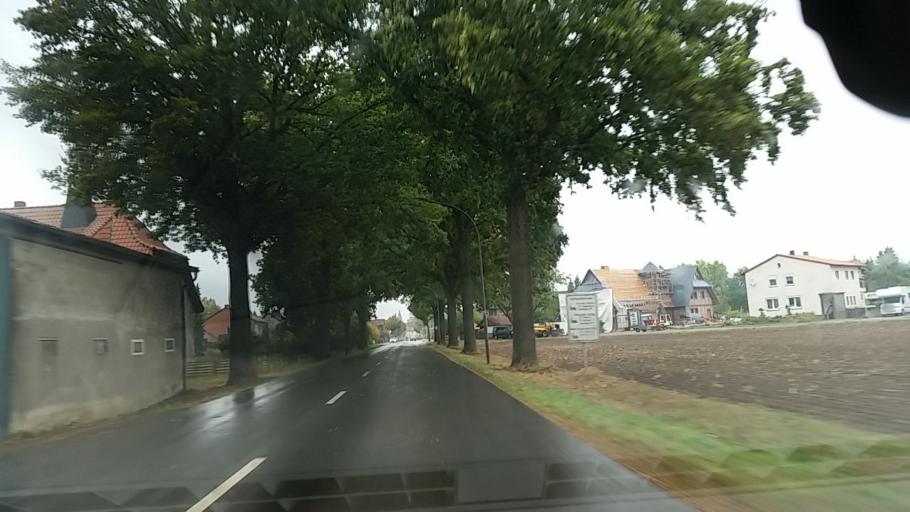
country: DE
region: Lower Saxony
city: Wittingen
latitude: 52.7237
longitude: 10.7510
